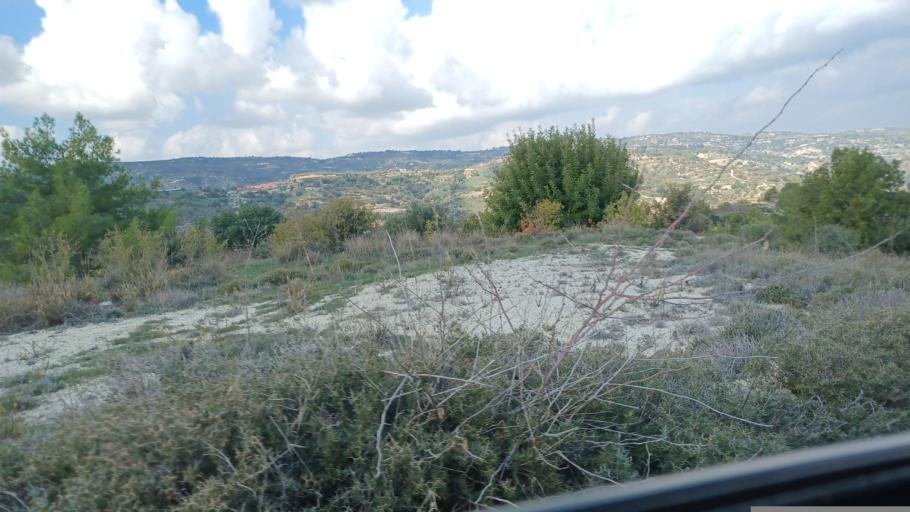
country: CY
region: Pafos
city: Mesogi
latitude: 34.8299
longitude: 32.5235
